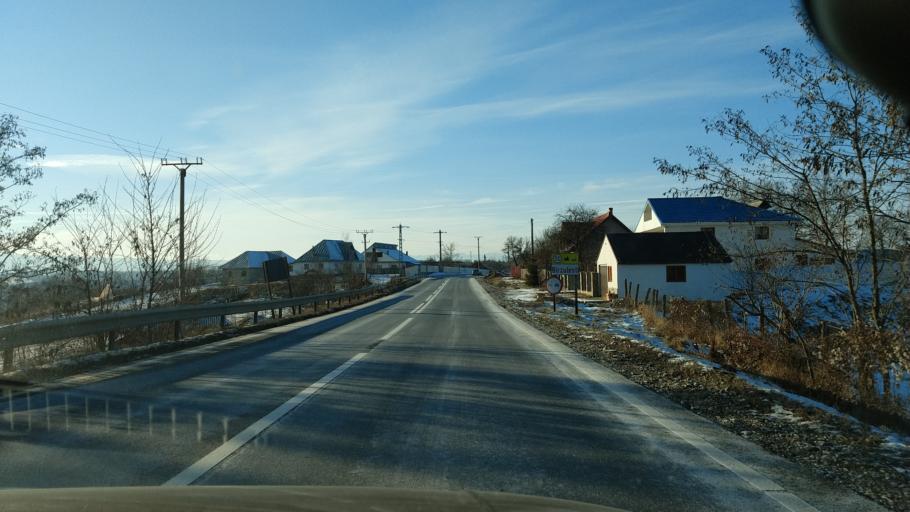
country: RO
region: Bacau
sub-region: Comuna Luizi-Calugara
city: Luizi-Calugara
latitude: 46.4920
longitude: 26.7863
